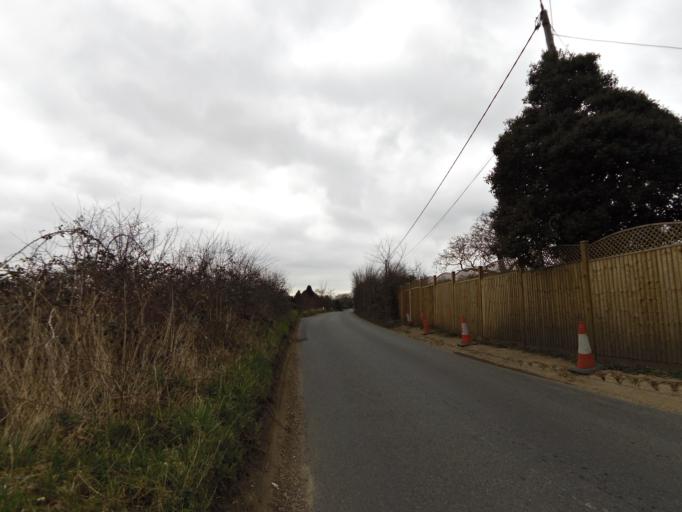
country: GB
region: England
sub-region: Suffolk
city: Ipswich
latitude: 52.1277
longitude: 1.1443
